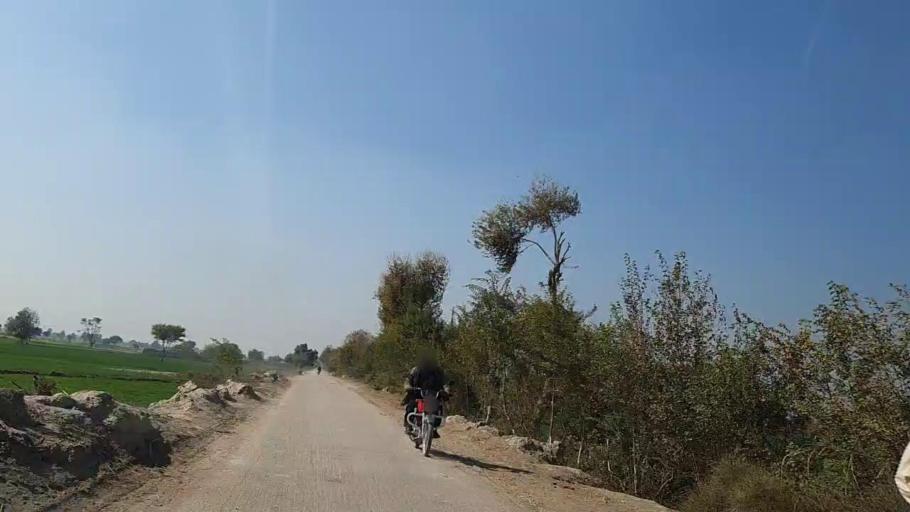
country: PK
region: Sindh
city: Daulatpur
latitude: 26.2905
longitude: 68.0764
